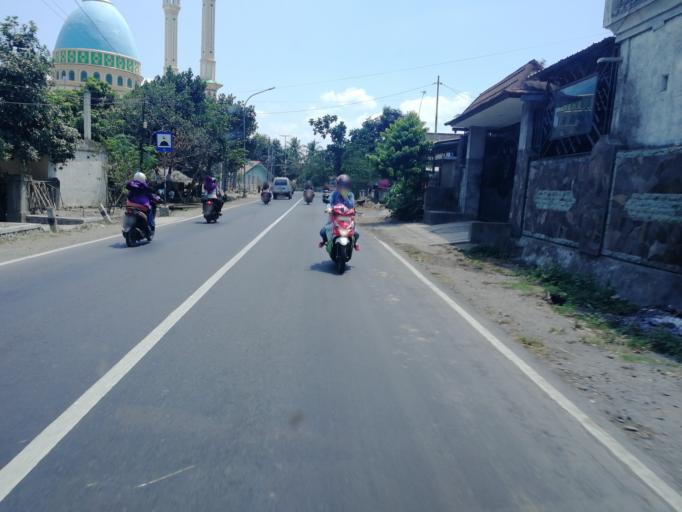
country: ID
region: West Nusa Tenggara
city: Jelateng Timur
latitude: -8.7083
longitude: 116.0785
